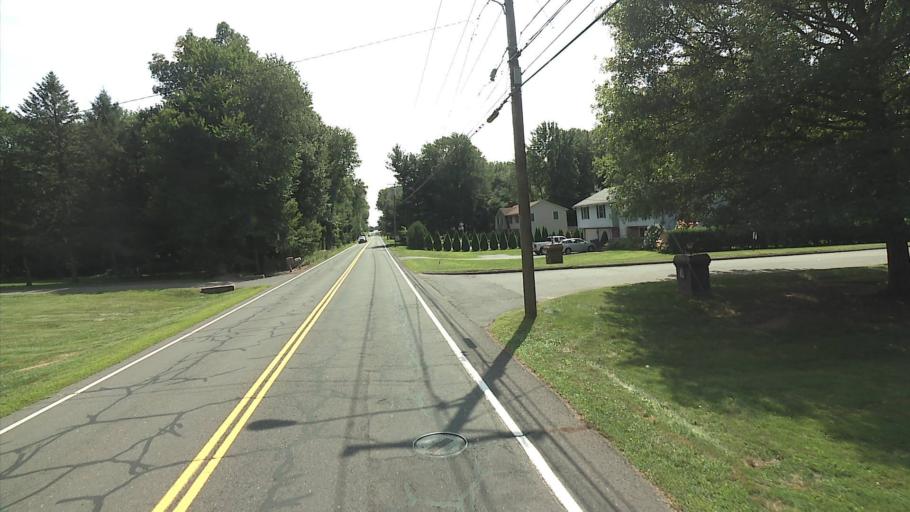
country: US
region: Connecticut
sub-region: Hartford County
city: Broad Brook
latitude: 41.9487
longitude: -72.5270
